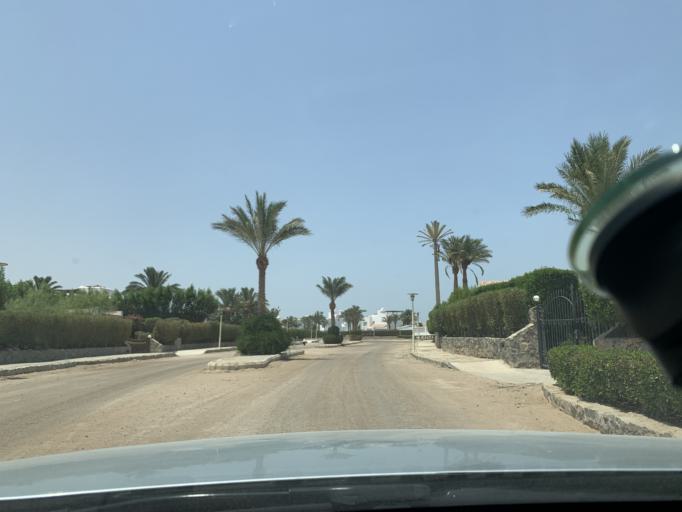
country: EG
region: Red Sea
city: El Gouna
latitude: 27.3703
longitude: 33.6707
